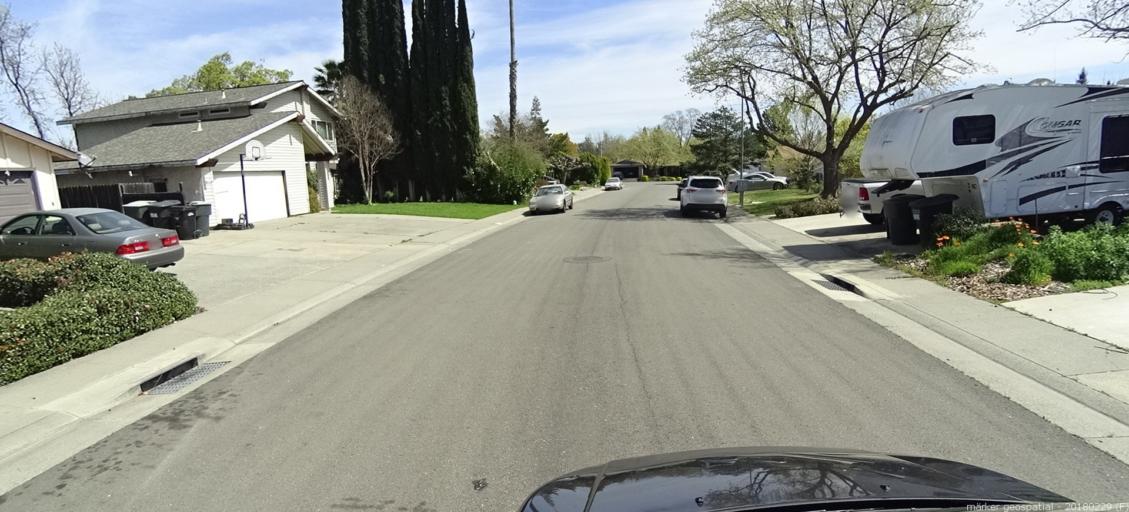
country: US
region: California
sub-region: Sacramento County
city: La Riviera
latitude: 38.5538
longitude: -121.3494
